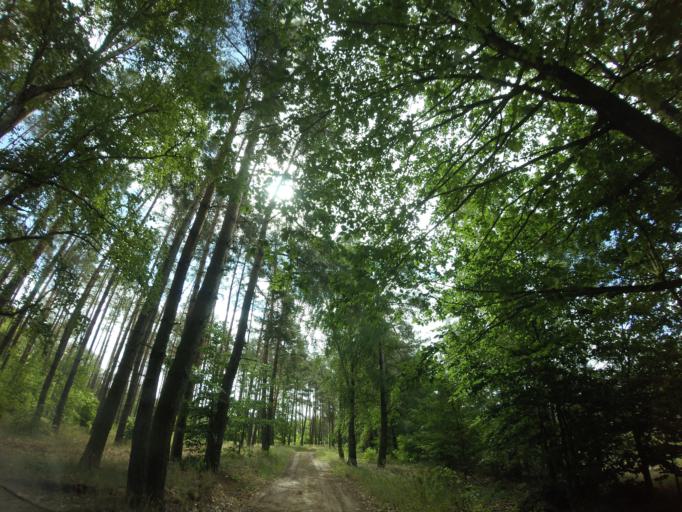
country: PL
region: West Pomeranian Voivodeship
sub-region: Powiat choszczenski
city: Bierzwnik
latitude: 53.0101
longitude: 15.6876
